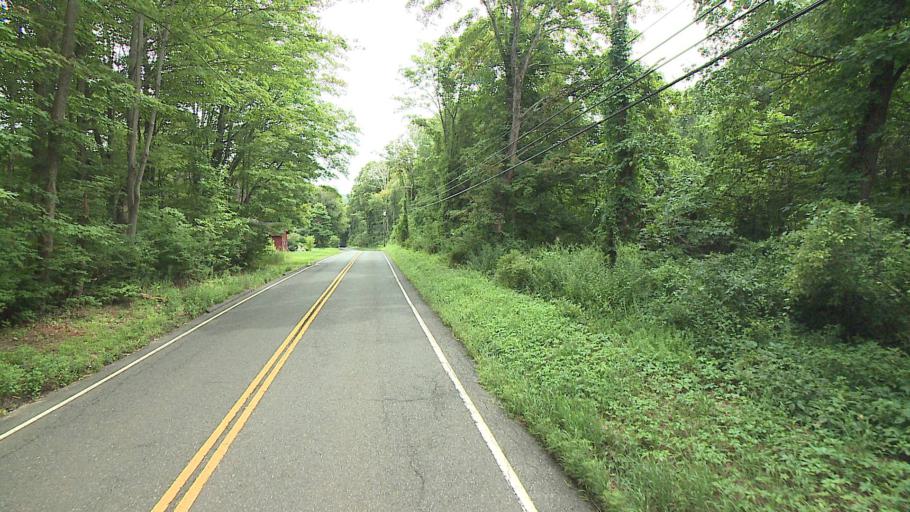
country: US
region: Connecticut
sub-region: Litchfield County
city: Woodbury
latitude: 41.5606
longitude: -73.2872
